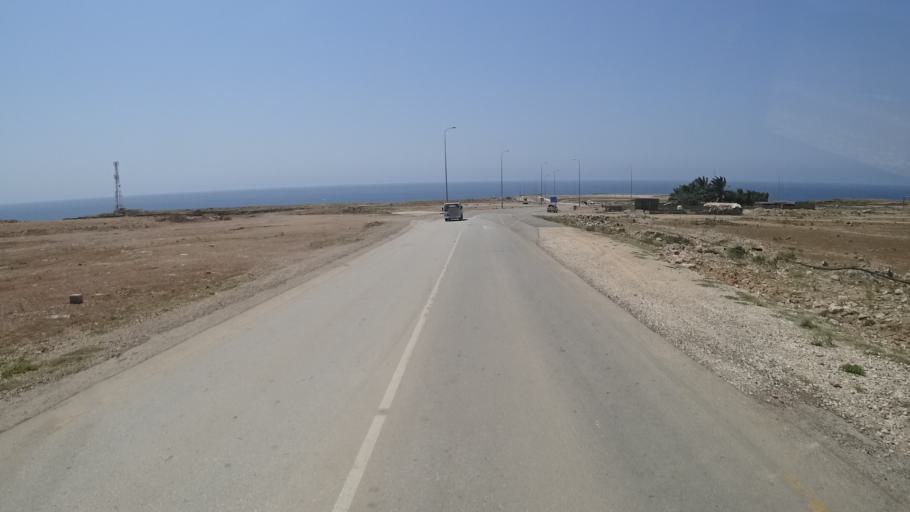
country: OM
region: Zufar
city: Salalah
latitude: 17.0346
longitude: 54.6126
